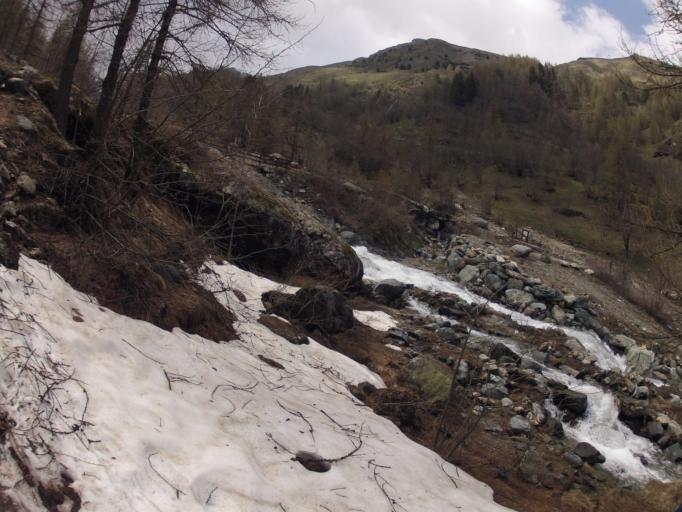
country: IT
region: Piedmont
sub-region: Provincia di Cuneo
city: Crissolo
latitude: 44.7009
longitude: 7.1342
